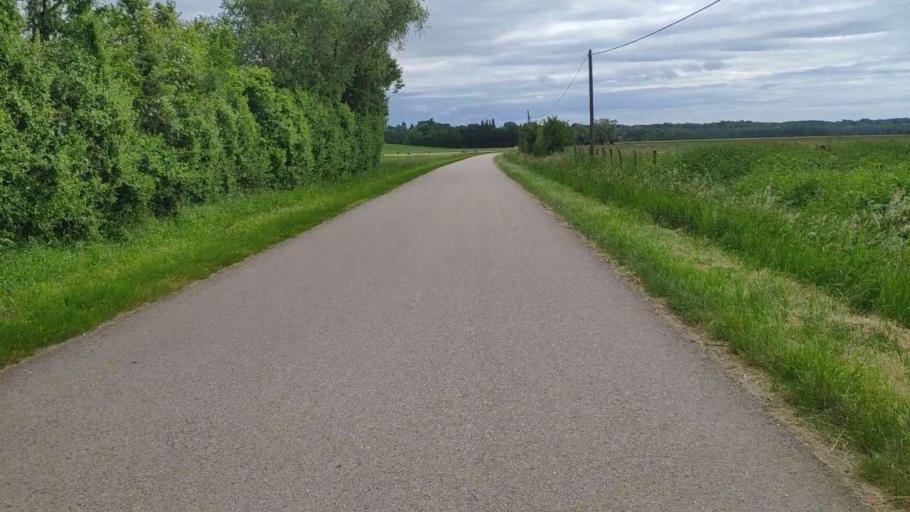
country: FR
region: Franche-Comte
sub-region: Departement du Jura
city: Bletterans
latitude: 46.7370
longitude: 5.4985
